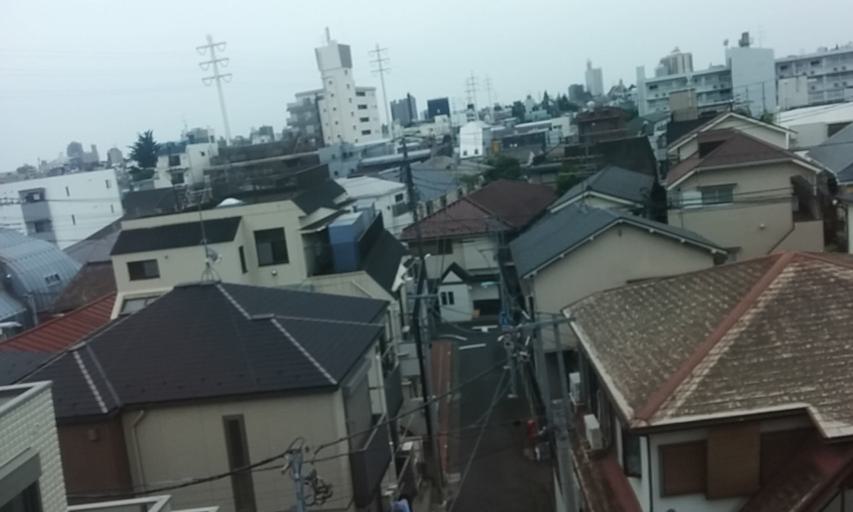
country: JP
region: Tokyo
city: Tokyo
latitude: 35.7051
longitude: 139.6454
